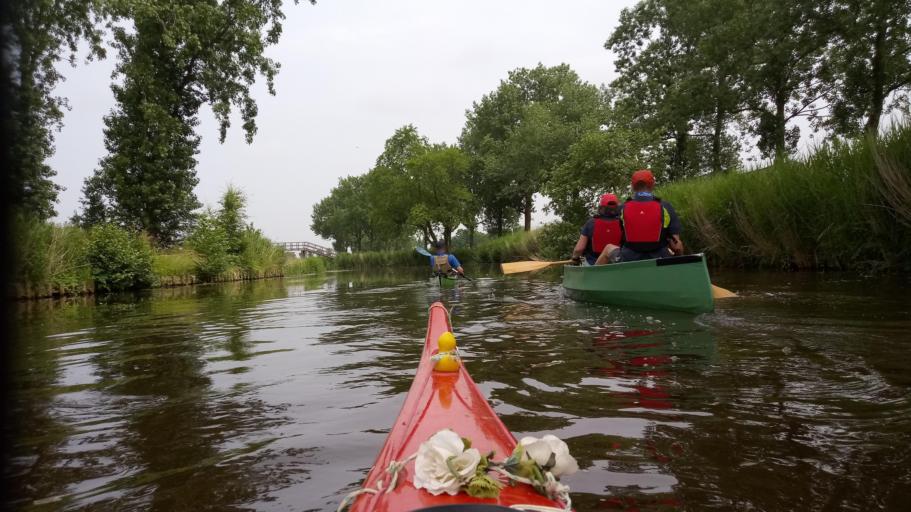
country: NL
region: Groningen
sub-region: Gemeente Bedum
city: Bedum
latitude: 53.3402
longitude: 6.5821
